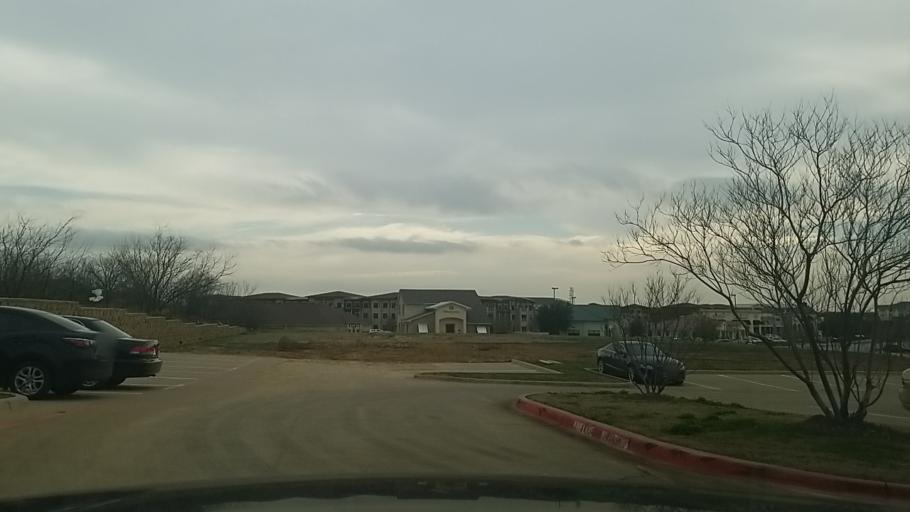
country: US
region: Texas
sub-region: Denton County
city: Corinth
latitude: 33.1758
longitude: -97.0952
